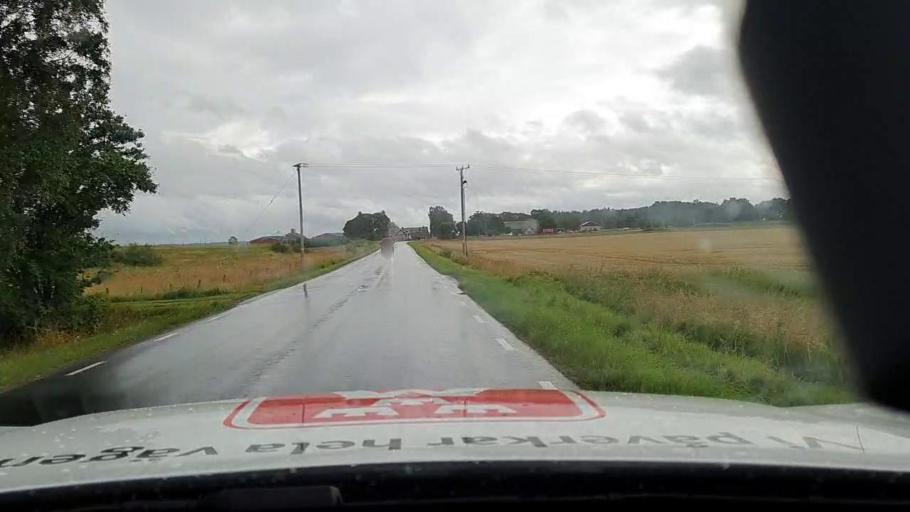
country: SE
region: Vaestra Goetaland
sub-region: Skovde Kommun
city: Stopen
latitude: 58.5574
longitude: 13.9808
